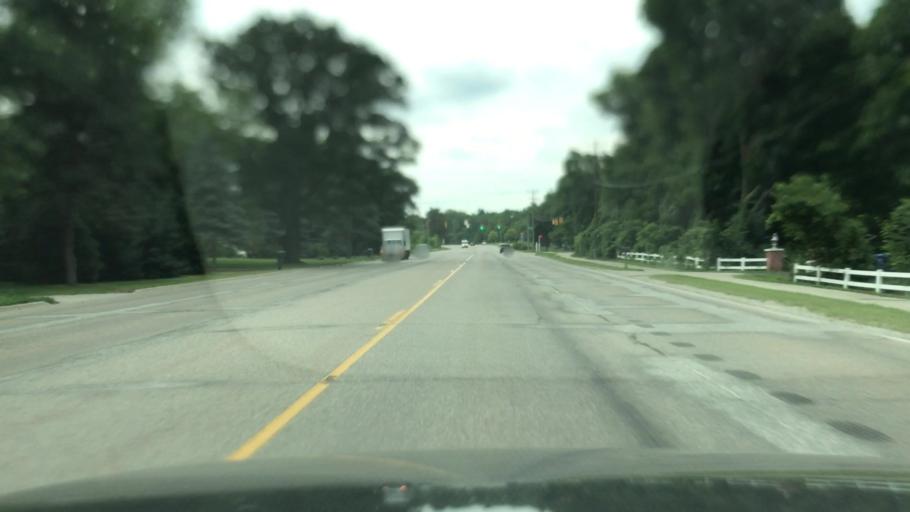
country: US
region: Michigan
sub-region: Kent County
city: Forest Hills
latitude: 42.9192
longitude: -85.5039
